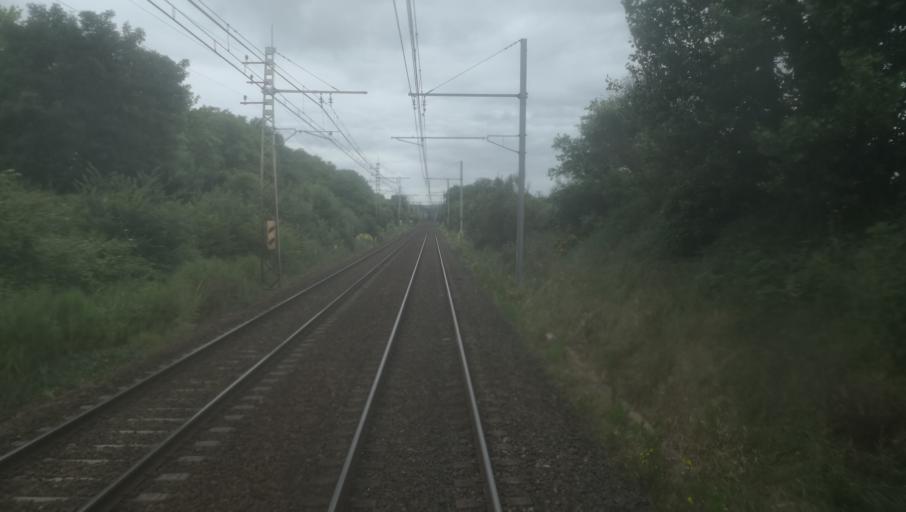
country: FR
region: Midi-Pyrenees
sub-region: Departement de la Haute-Garonne
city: Saint-Jory
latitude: 43.7539
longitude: 1.3617
